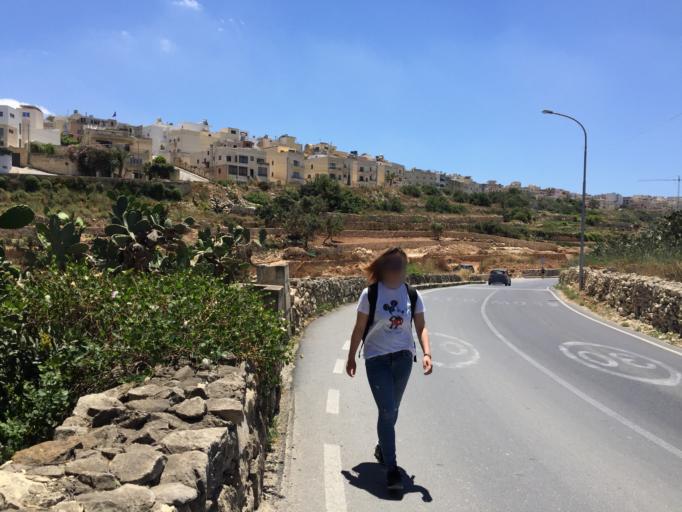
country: MT
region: Is-Swieqi
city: Swieqi
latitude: 35.9173
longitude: 14.4804
